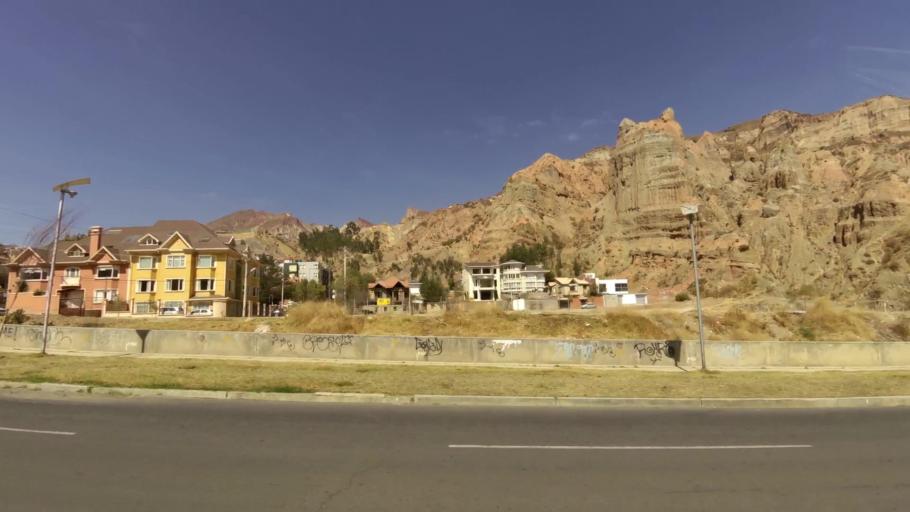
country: BO
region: La Paz
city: La Paz
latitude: -16.5464
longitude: -68.0595
